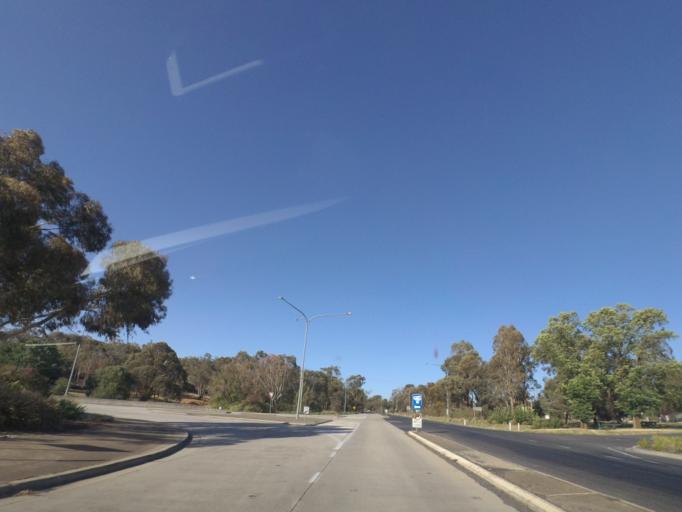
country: AU
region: New South Wales
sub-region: Wagga Wagga
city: Forest Hill
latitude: -35.2758
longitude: 147.7387
